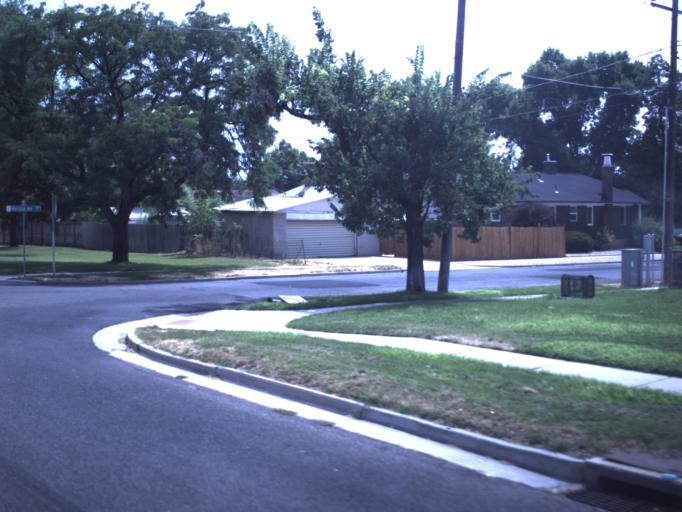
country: US
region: Utah
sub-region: Salt Lake County
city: South Salt Lake
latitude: 40.7403
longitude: -111.8713
